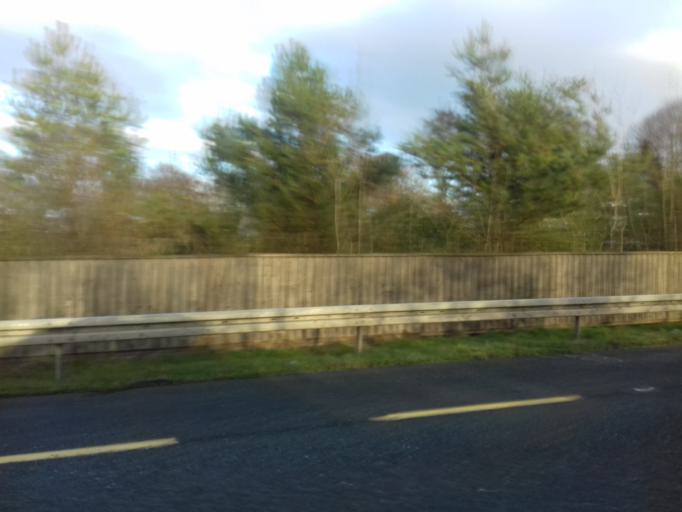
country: IE
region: Ulster
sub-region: County Monaghan
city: Carrickmacross
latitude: 53.9591
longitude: -6.6806
